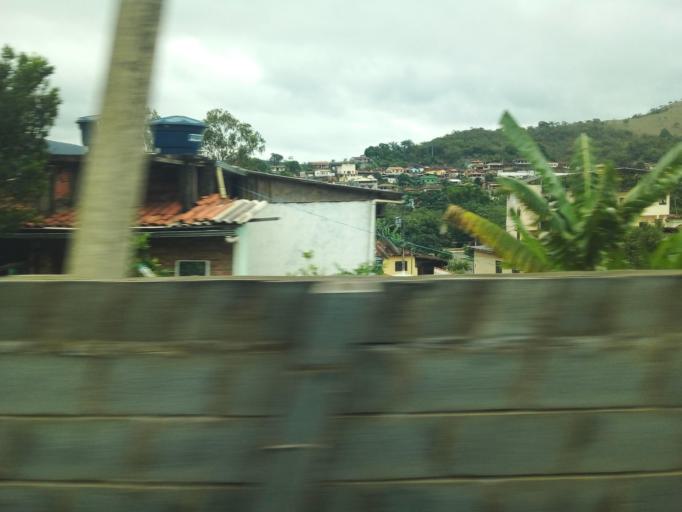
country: BR
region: Minas Gerais
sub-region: Rio Piracicaba
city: Rio Piracicaba
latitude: -19.9375
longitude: -43.1726
